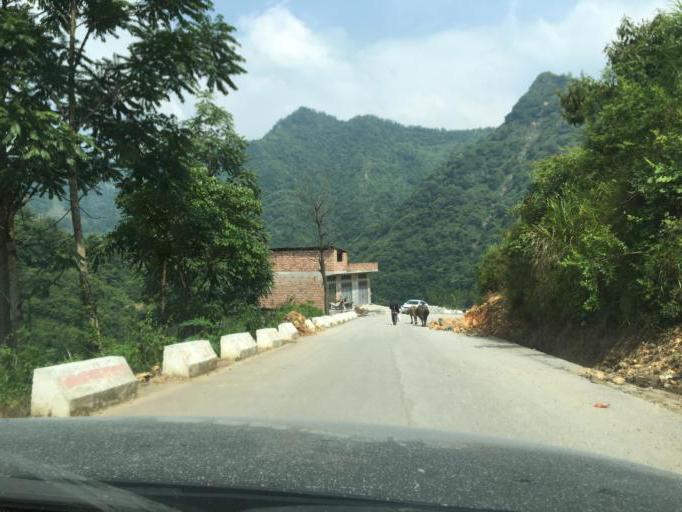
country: CN
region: Guangxi Zhuangzu Zizhiqu
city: Tongle
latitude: 25.2963
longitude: 106.2660
